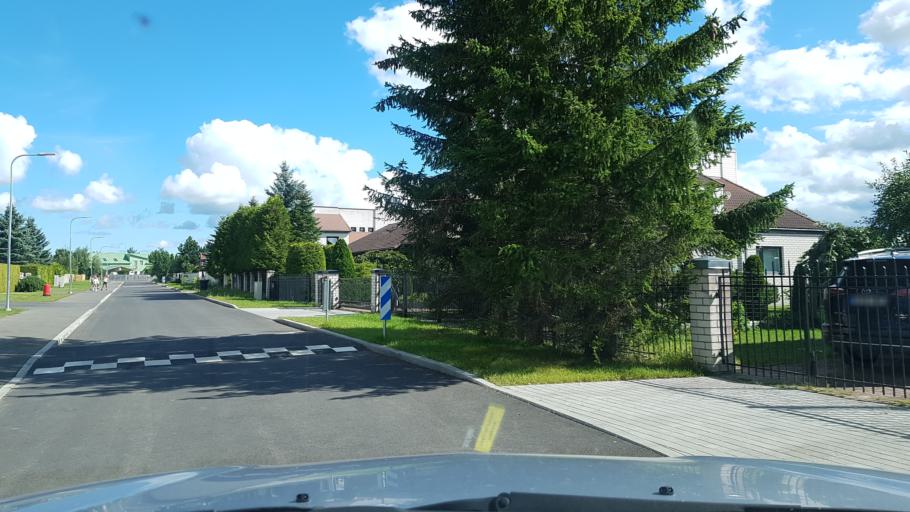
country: EE
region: Harju
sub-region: Tallinna linn
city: Tallinn
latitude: 59.3867
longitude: 24.7961
